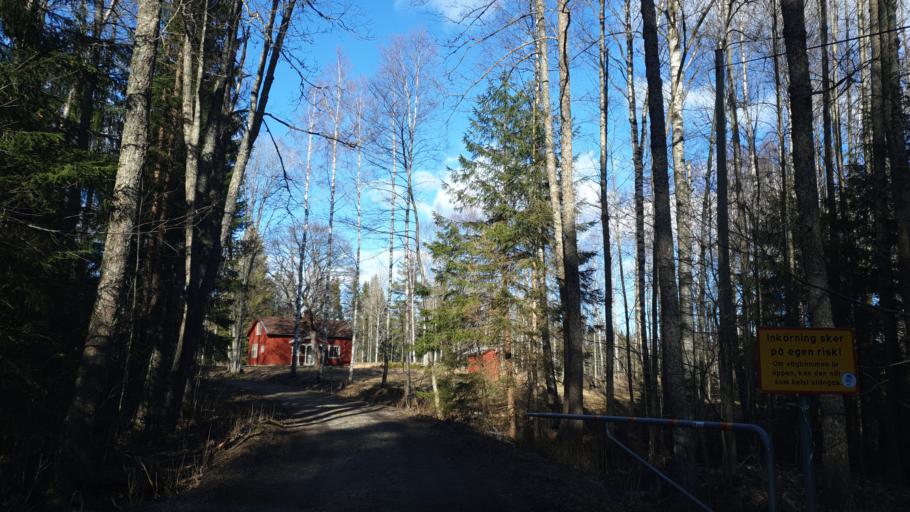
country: SE
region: OErebro
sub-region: Orebro Kommun
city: Garphyttan
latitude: 59.3682
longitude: 14.9676
